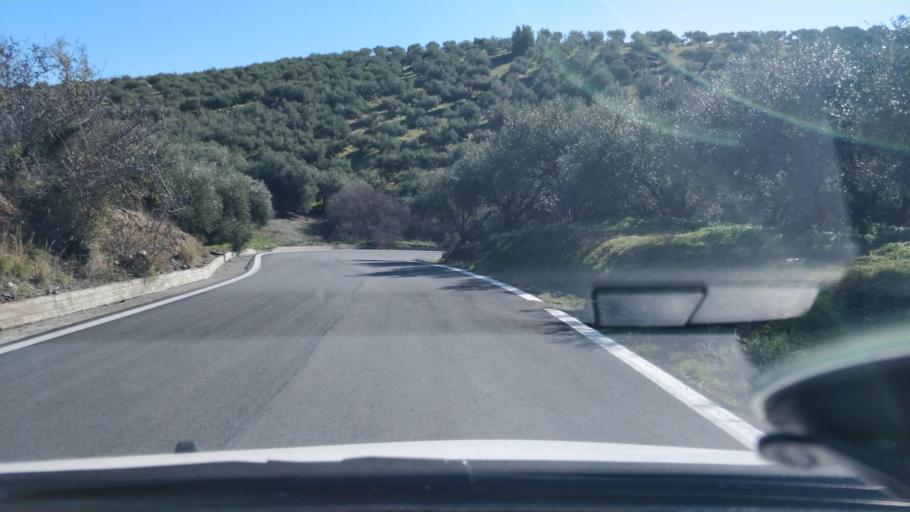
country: GR
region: Crete
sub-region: Nomos Irakleiou
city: Arkalochori
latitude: 35.0061
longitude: 25.4406
